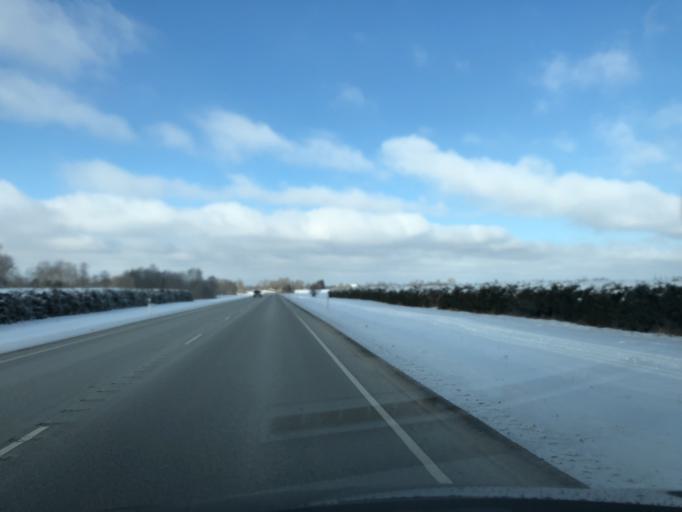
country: EE
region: Jaervamaa
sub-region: Paide linn
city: Paide
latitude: 58.8563
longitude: 25.7210
